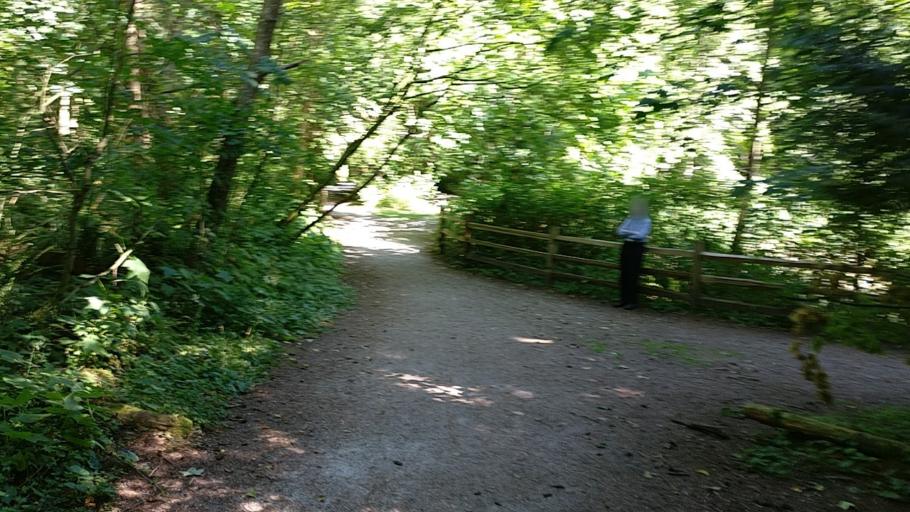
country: CA
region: British Columbia
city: Surrey
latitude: 49.0501
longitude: -122.8626
